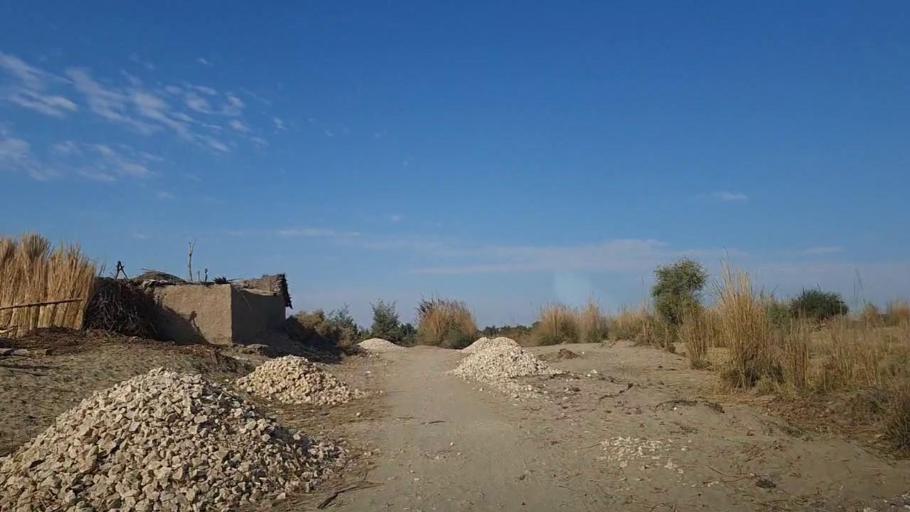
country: PK
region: Sindh
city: Jam Sahib
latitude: 26.3135
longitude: 68.8141
